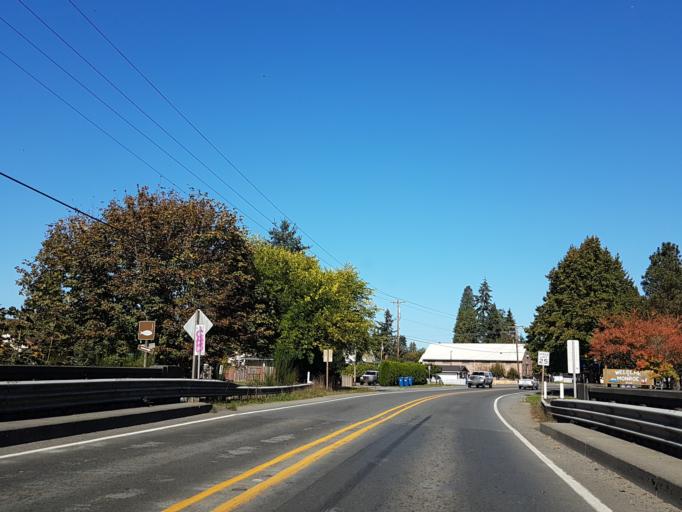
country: US
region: Washington
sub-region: Snohomish County
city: Monroe
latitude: 47.8467
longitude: -121.9709
